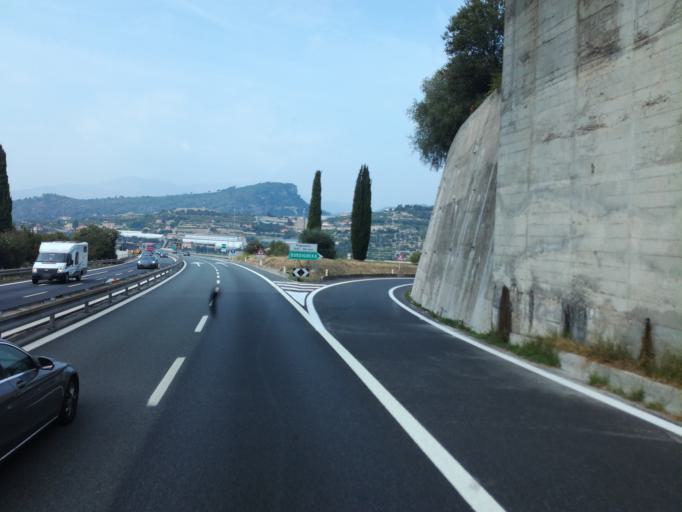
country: IT
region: Liguria
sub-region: Provincia di Imperia
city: Vallebona
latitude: 43.7994
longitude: 7.6692
